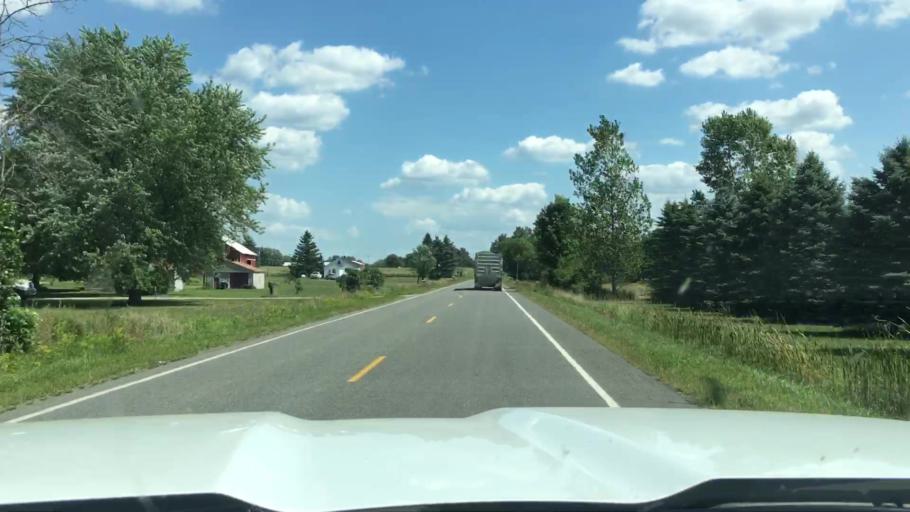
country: US
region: Michigan
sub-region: Muskegon County
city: Ravenna
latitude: 43.2795
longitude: -85.9179
